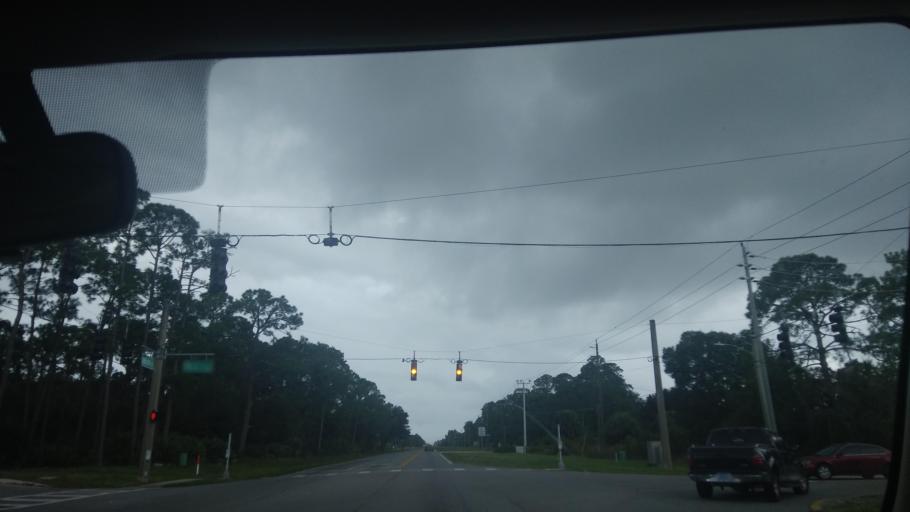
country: US
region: Florida
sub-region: Brevard County
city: Grant-Valkaria
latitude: 27.9664
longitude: -80.6226
